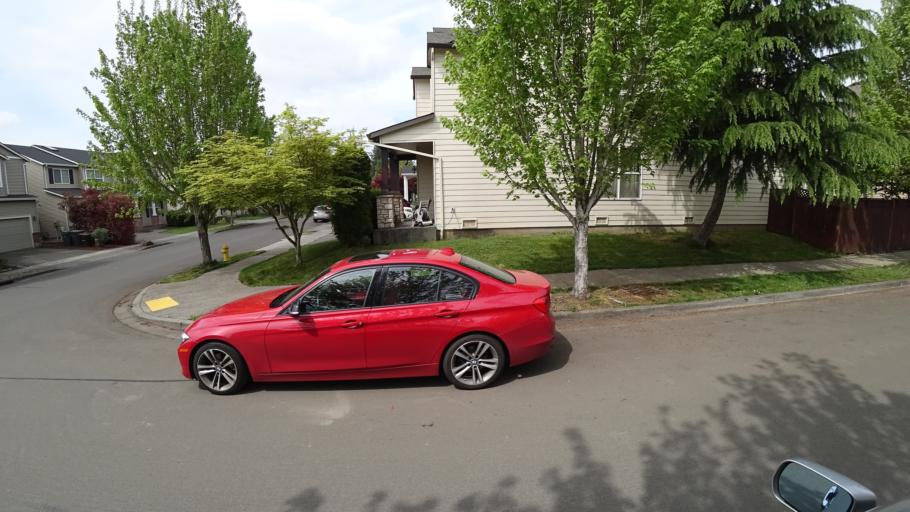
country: US
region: Oregon
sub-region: Washington County
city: Hillsboro
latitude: 45.5352
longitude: -122.9979
